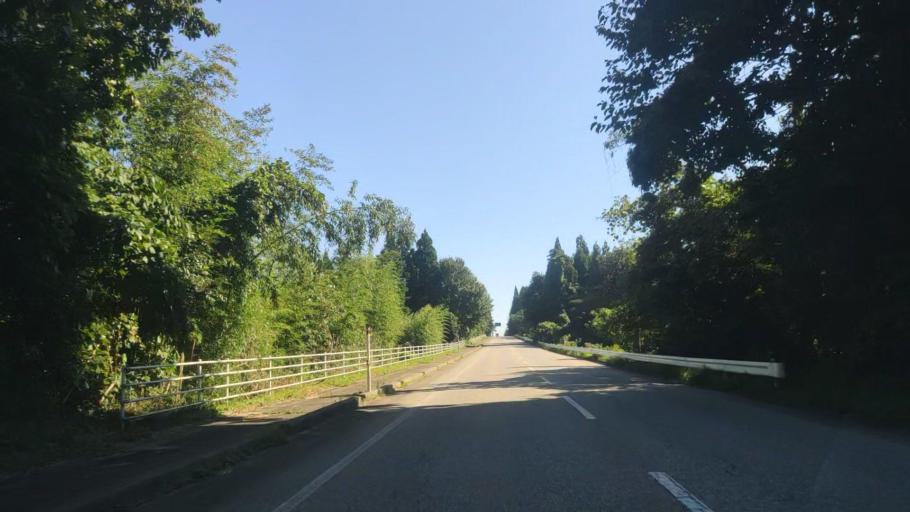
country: JP
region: Ishikawa
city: Nanao
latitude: 37.3728
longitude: 137.2350
